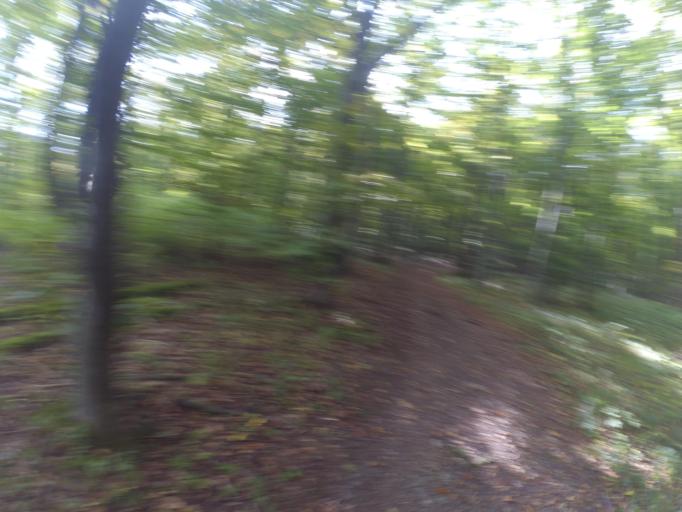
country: DE
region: Baden-Wuerttemberg
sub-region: Regierungsbezirk Stuttgart
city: Heubach
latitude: 48.7820
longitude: 9.9189
